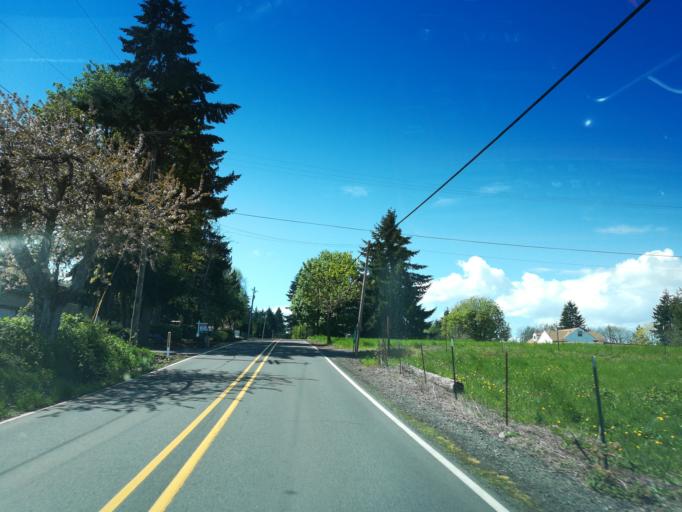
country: US
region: Oregon
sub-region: Clackamas County
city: Damascus
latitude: 45.4325
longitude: -122.4290
